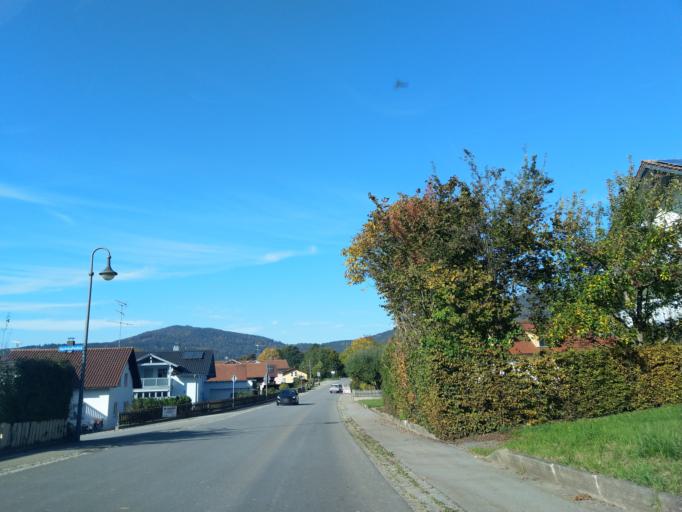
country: DE
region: Bavaria
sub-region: Lower Bavaria
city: Metten
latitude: 48.8989
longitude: 12.9245
